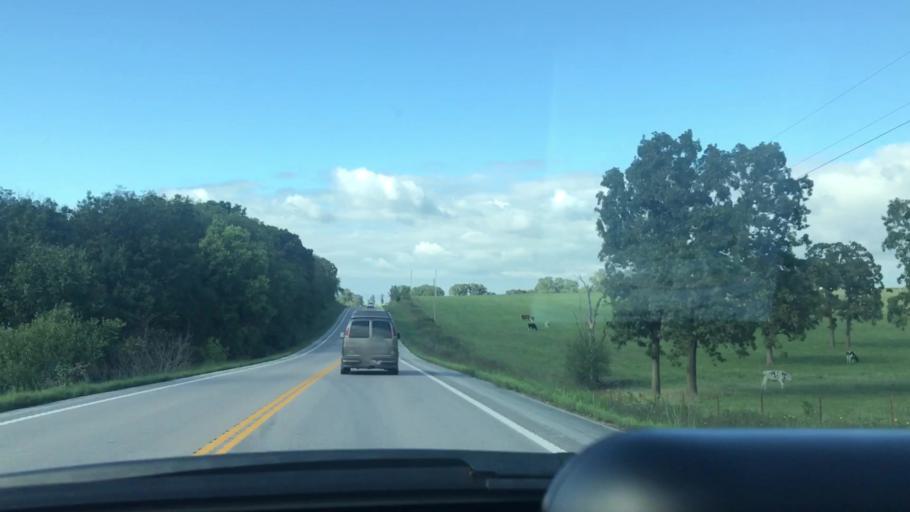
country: US
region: Missouri
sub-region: Hickory County
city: Hermitage
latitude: 37.9745
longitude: -93.2062
